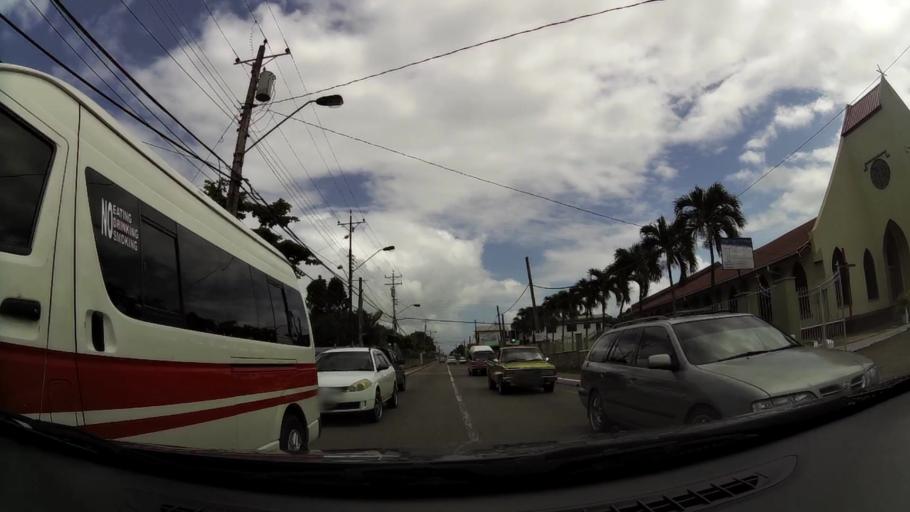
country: TT
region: Tunapuna/Piarco
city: Arouca
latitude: 10.6338
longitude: -61.3356
